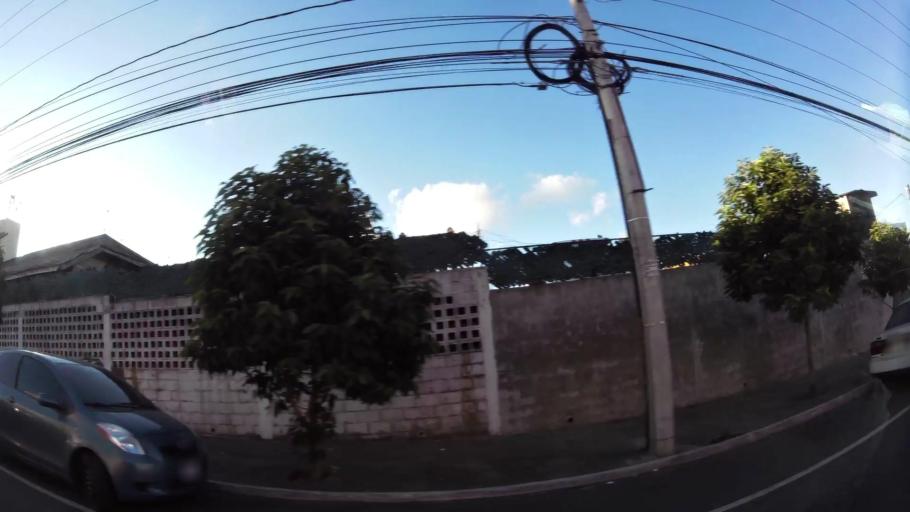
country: GT
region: Guatemala
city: Guatemala City
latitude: 14.6149
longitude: -90.5286
